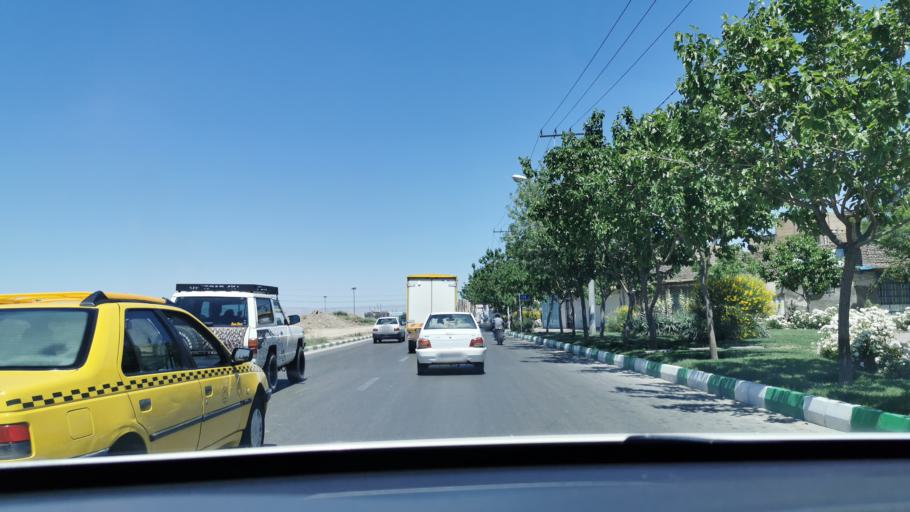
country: IR
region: Razavi Khorasan
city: Mashhad
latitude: 36.2598
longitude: 59.6473
